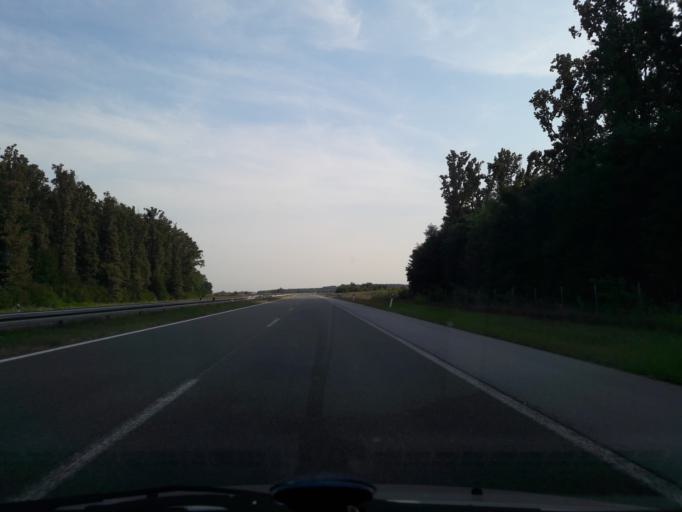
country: HR
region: Osjecko-Baranjska
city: Vuka
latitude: 45.4393
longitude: 18.4604
